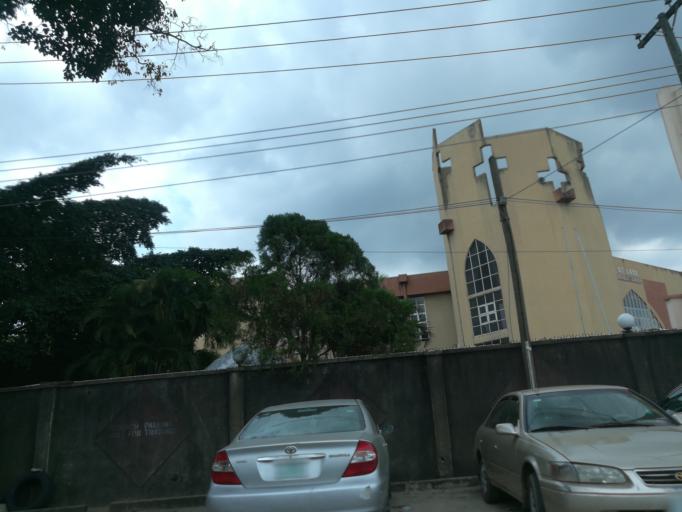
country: NG
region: Lagos
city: Ikeja
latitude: 6.5969
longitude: 3.3499
